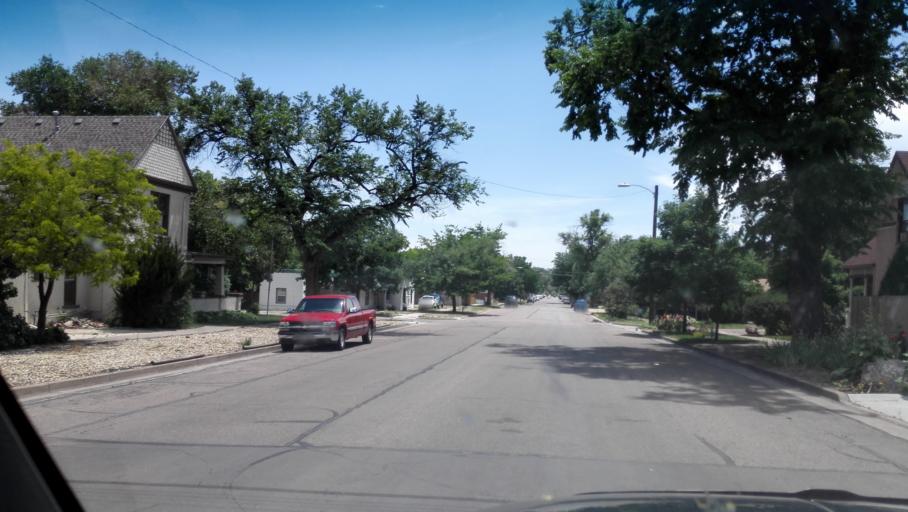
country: US
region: Colorado
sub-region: Fremont County
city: Canon City
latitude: 38.4442
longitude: -105.2436
